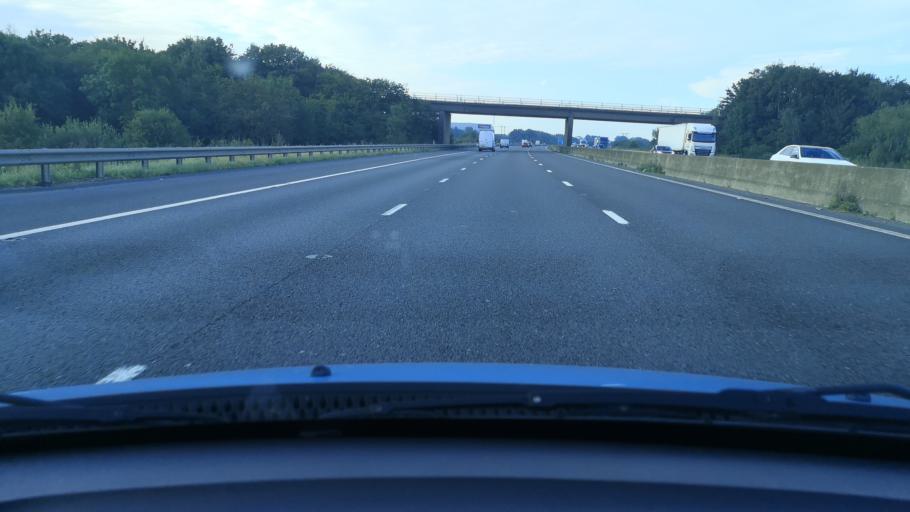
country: GB
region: England
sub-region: East Riding of Yorkshire
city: Rawcliffe
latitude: 53.6346
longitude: -0.9660
